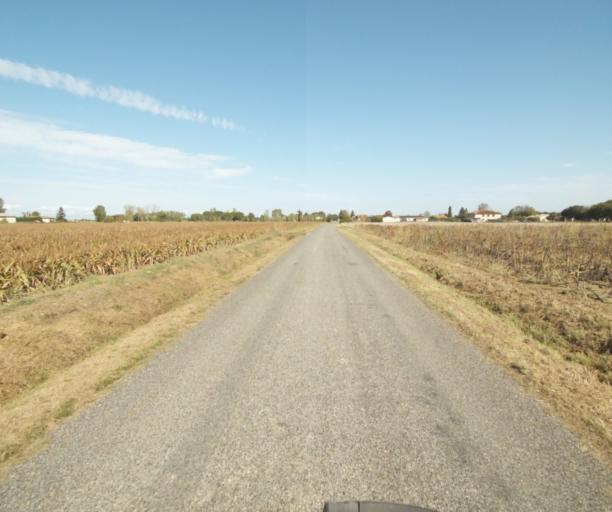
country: FR
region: Midi-Pyrenees
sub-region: Departement du Tarn-et-Garonne
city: Verdun-sur-Garonne
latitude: 43.8520
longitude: 1.2077
